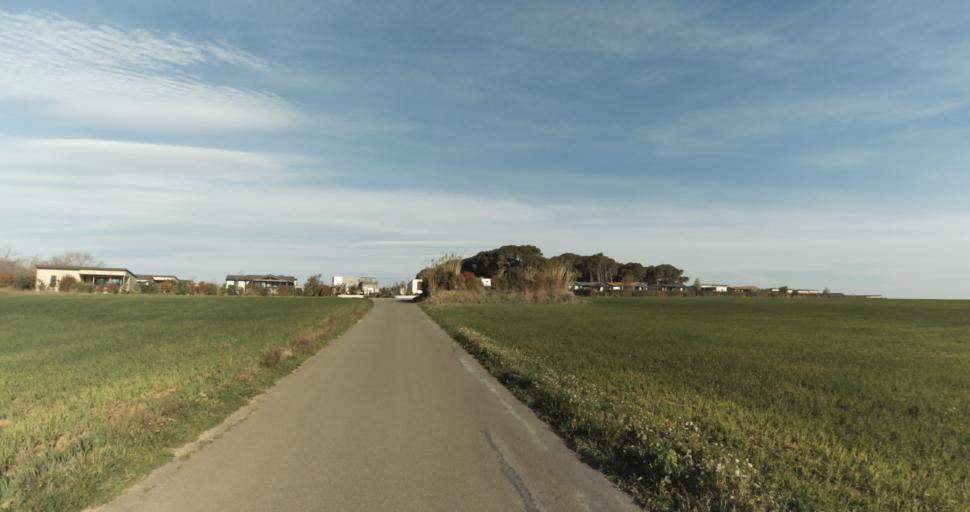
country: FR
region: Languedoc-Roussillon
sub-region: Departement de l'Herault
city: Pomerols
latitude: 43.3836
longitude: 3.5199
